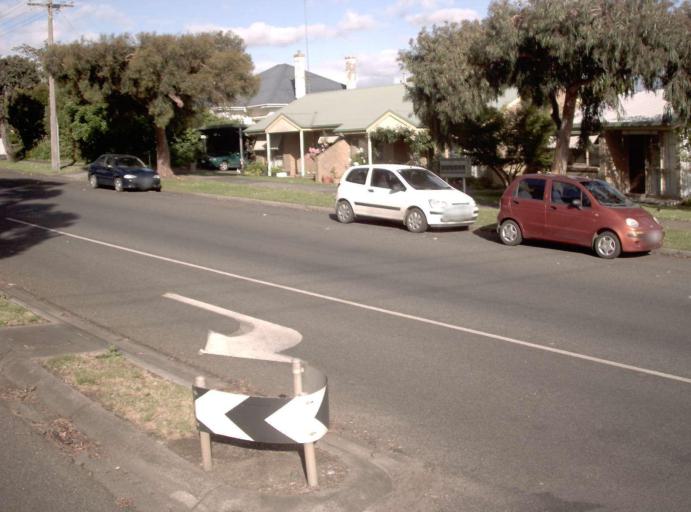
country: AU
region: Victoria
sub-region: Baw Baw
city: Warragul
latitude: -38.4791
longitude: 145.9420
